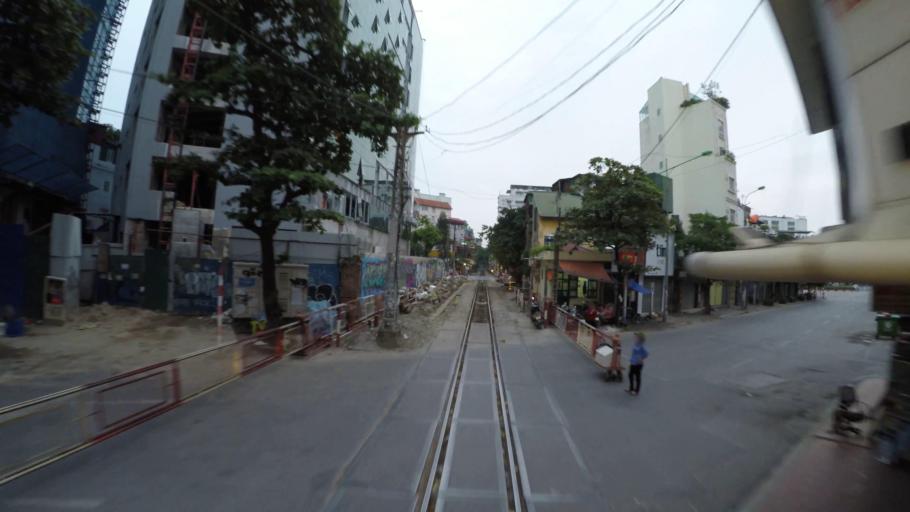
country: VN
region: Ha Noi
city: Hoan Kiem
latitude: 21.0358
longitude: 105.8458
